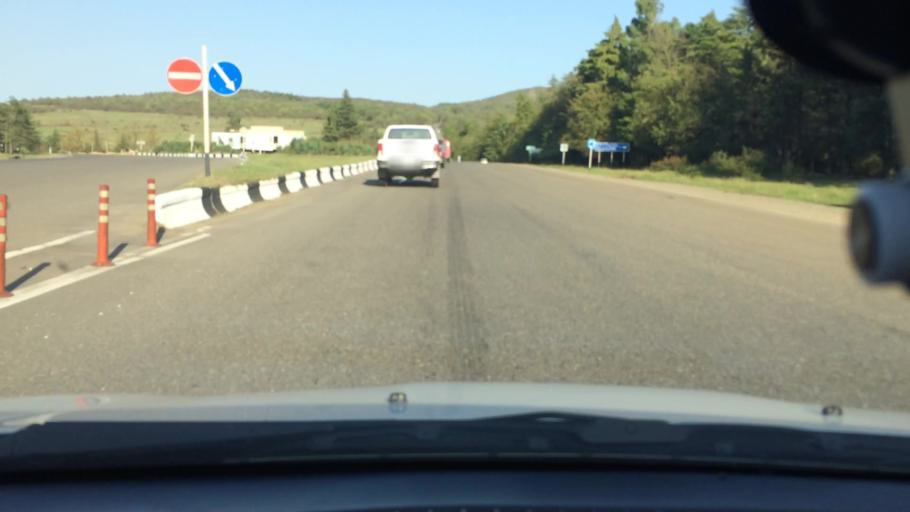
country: GE
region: Imereti
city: Kutaisi
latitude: 42.2390
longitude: 42.7672
